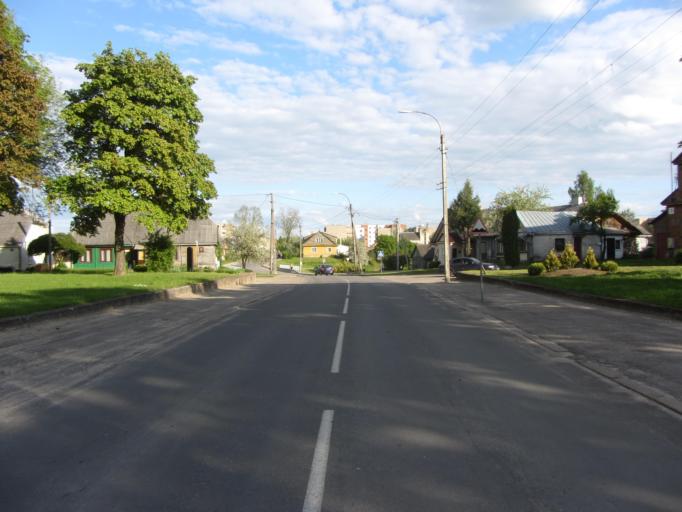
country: LT
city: Sirvintos
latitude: 55.0472
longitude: 24.9496
